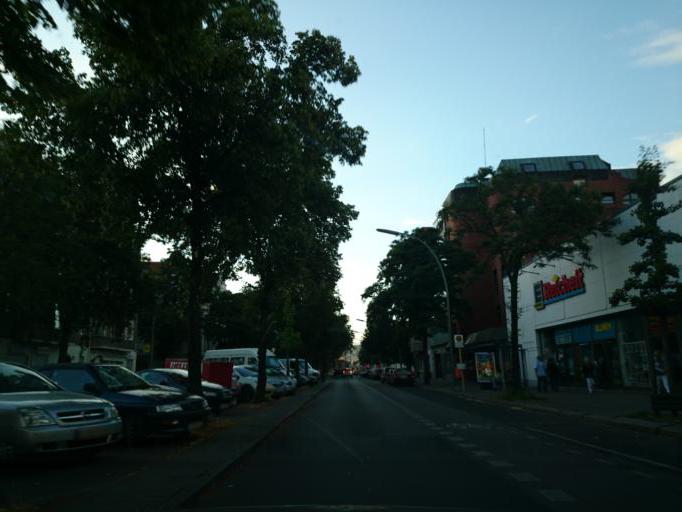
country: DE
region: Berlin
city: Wedding Bezirk
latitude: 52.5607
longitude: 13.3650
